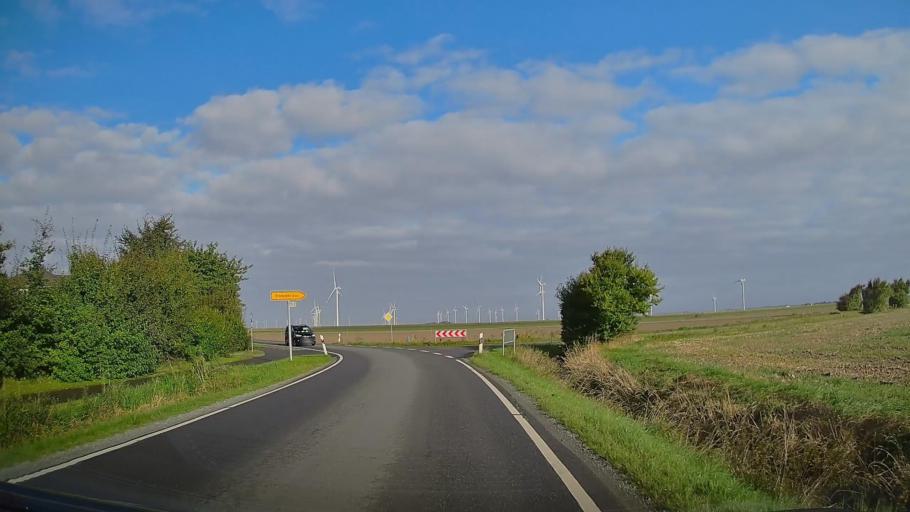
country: DE
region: Schleswig-Holstein
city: Reussenkoge
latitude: 54.5852
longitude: 8.9242
